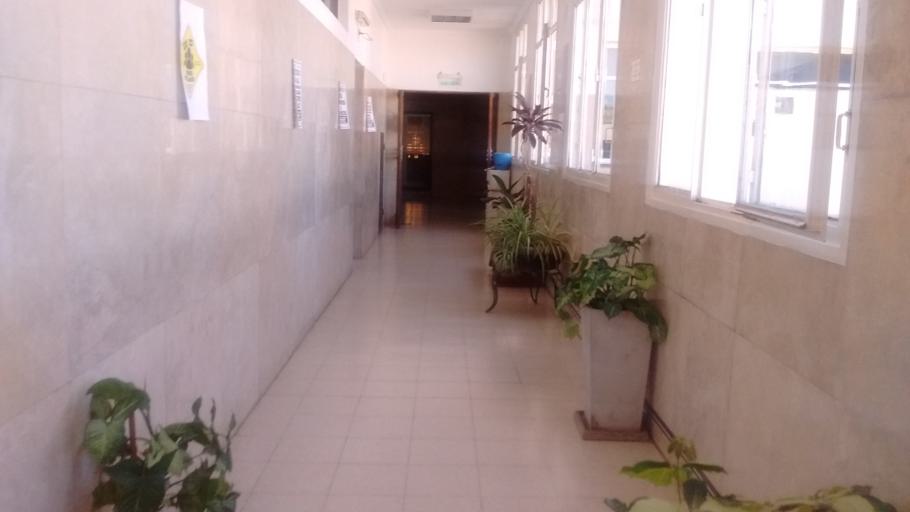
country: AR
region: Santa Fe
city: Santa Fe de la Vera Cruz
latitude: -31.6511
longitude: -60.7058
